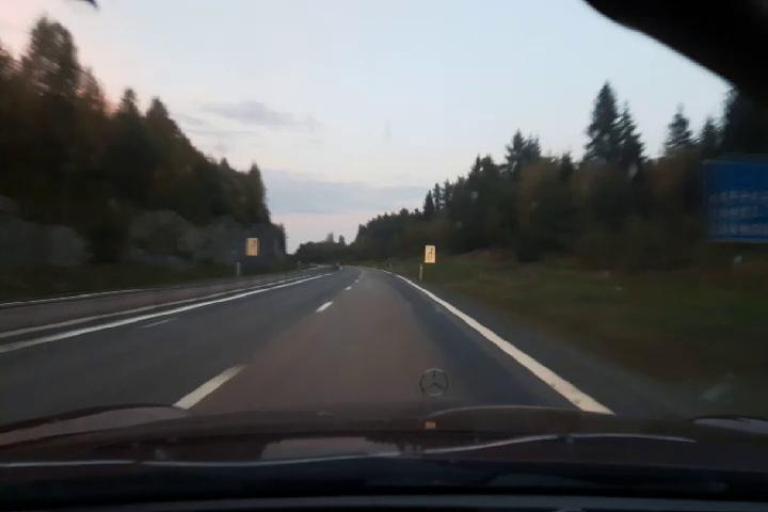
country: SE
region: Vaesternorrland
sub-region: Haernoesands Kommun
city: Haernoesand
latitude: 62.8653
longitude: 18.0362
